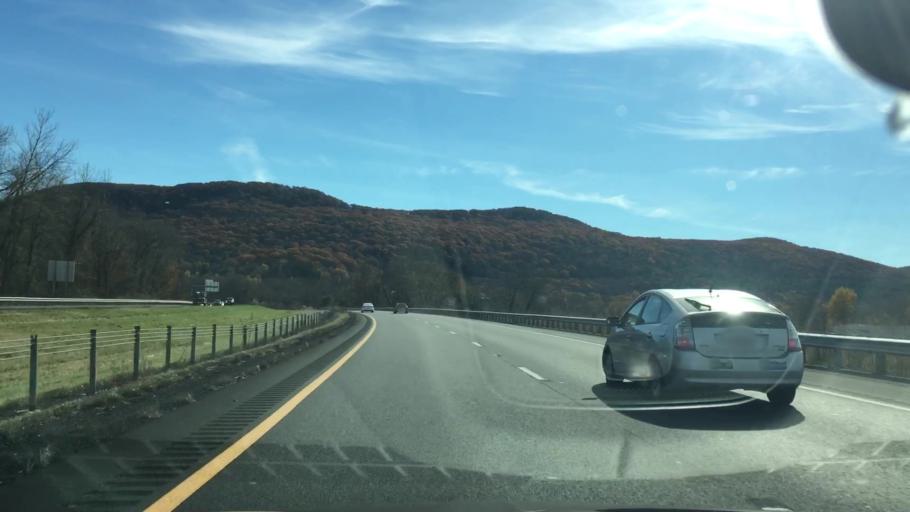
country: US
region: Massachusetts
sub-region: Hampshire County
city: Northampton
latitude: 42.2939
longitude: -72.6293
